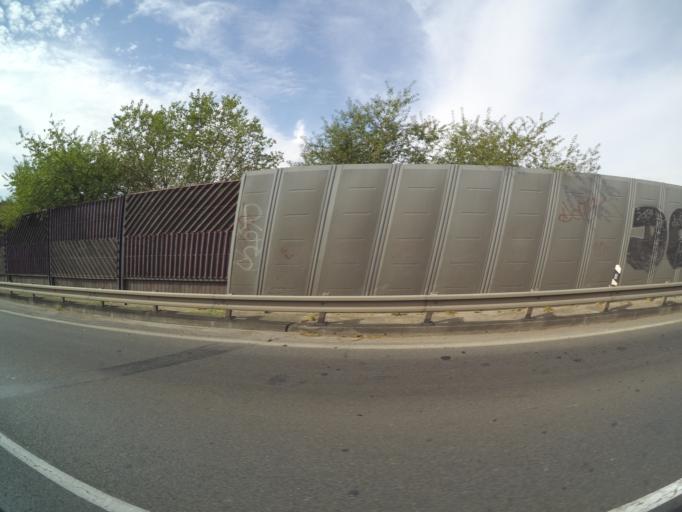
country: FR
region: Pays de la Loire
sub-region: Departement de Maine-et-Loire
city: Saumur
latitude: 47.2597
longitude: -0.0973
